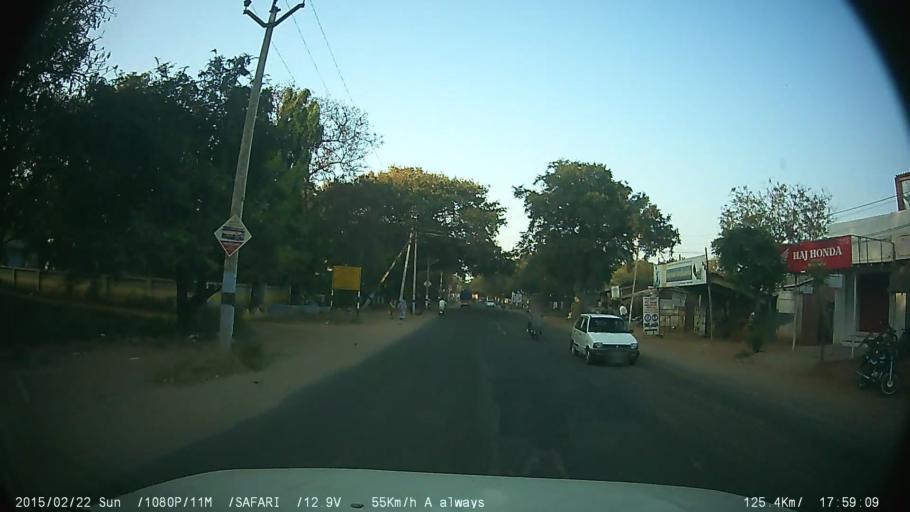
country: IN
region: Tamil Nadu
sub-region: Theni
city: Uttamapalaiyam
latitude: 9.7990
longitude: 77.3274
